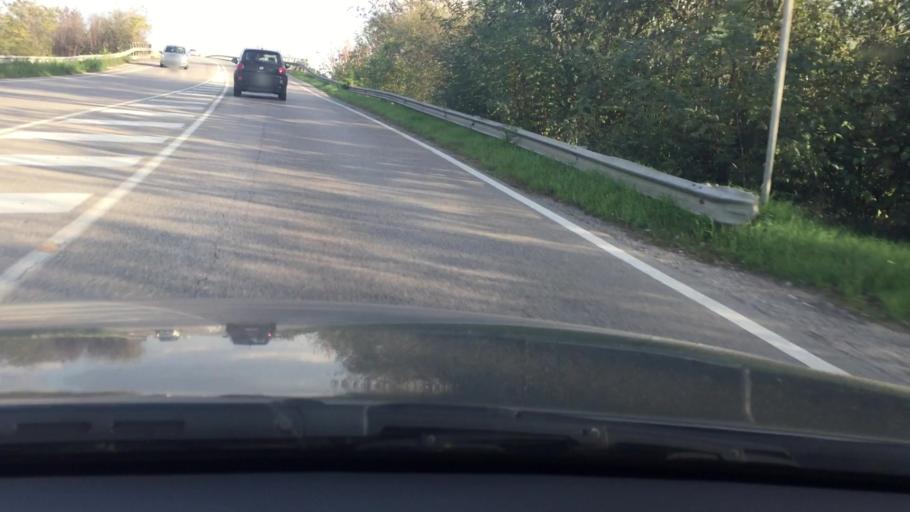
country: IT
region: Emilia-Romagna
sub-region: Provincia di Ferrara
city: Ferrara
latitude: 44.8162
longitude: 11.6124
